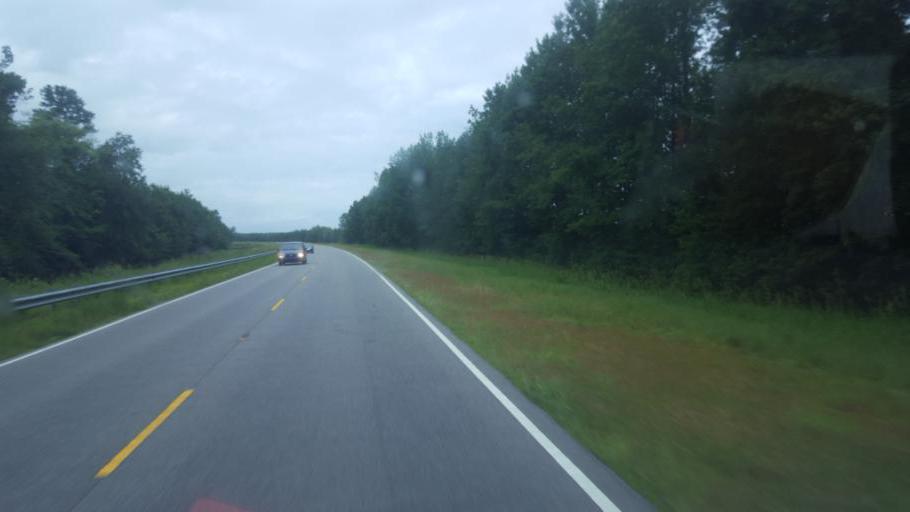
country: US
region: North Carolina
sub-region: Tyrrell County
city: Columbia
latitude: 35.9323
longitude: -76.1494
